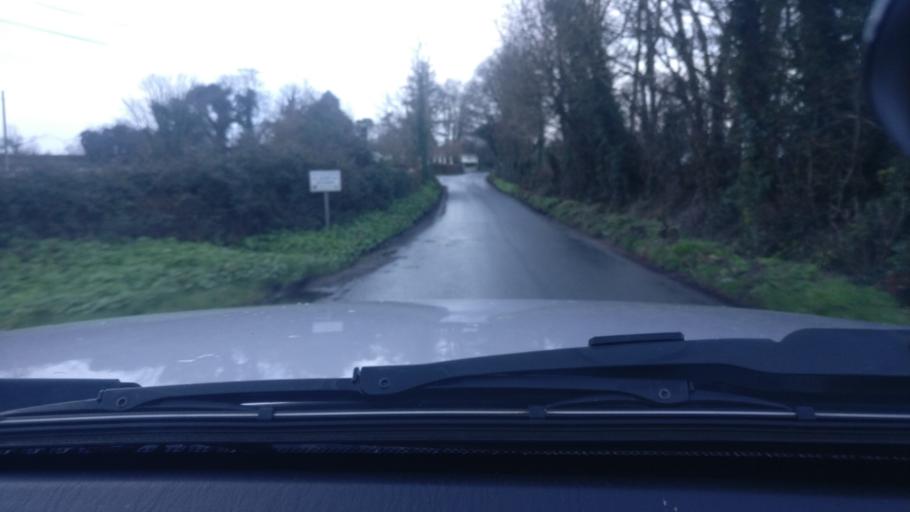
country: IE
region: Connaught
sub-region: County Galway
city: Loughrea
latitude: 53.1618
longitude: -8.5198
